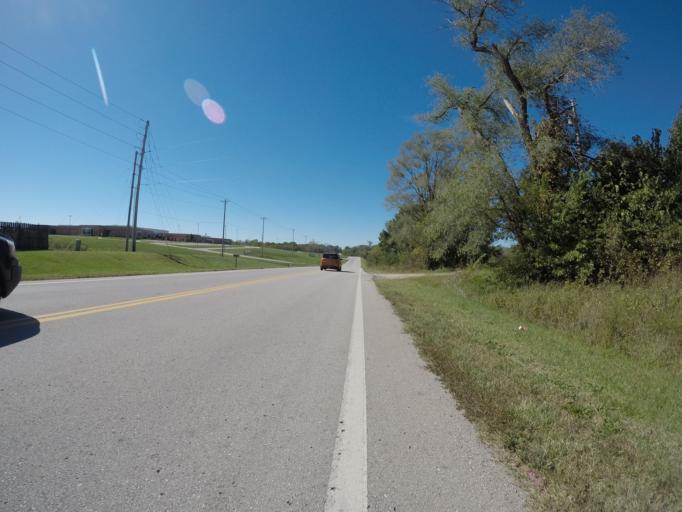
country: US
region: Kansas
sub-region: Douglas County
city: Eudora
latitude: 38.9425
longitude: -95.0851
